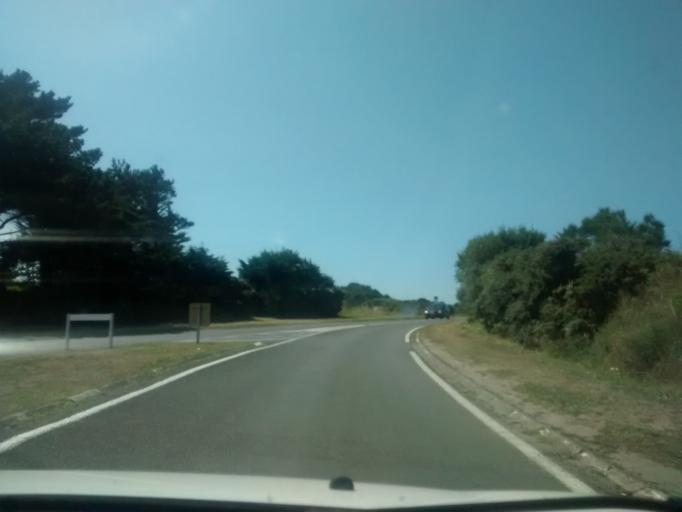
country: FR
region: Brittany
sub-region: Departement d'Ille-et-Vilaine
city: Cancale
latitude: 48.7052
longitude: -1.8491
